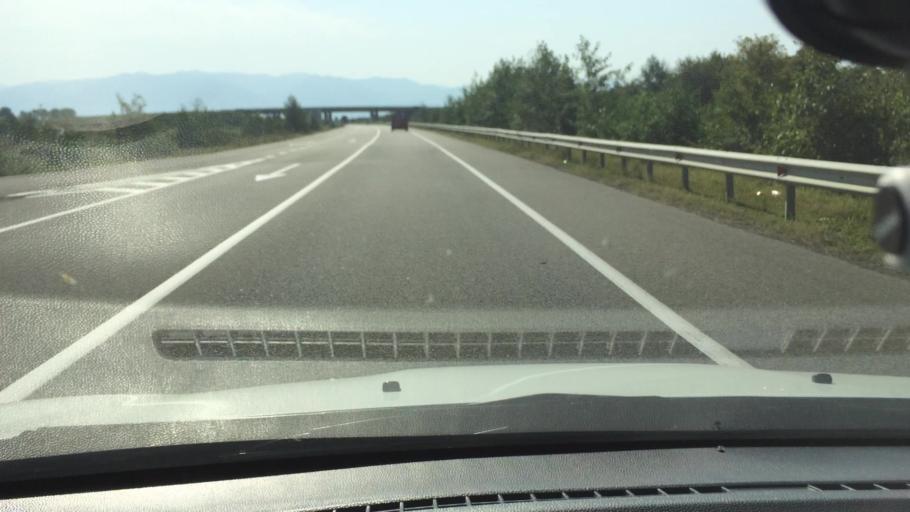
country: GE
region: Guria
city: Urek'i
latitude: 41.9210
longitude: 41.7745
